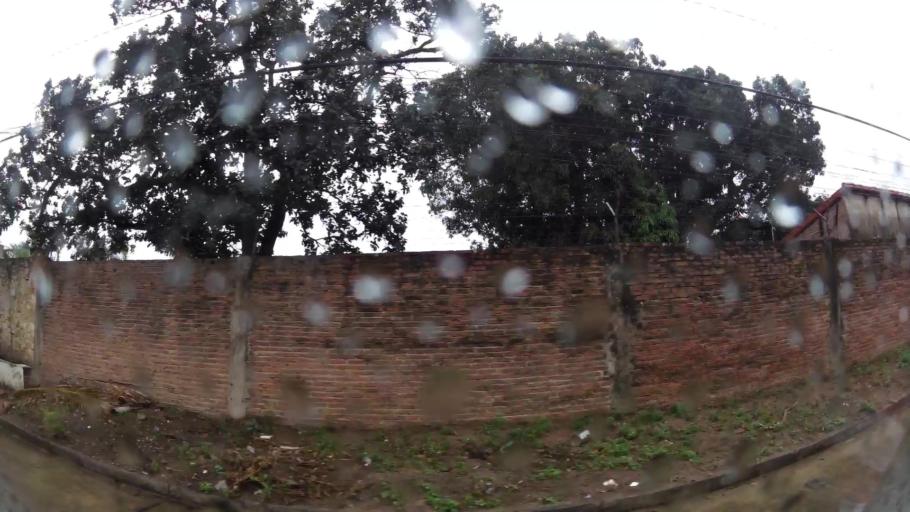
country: BO
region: Santa Cruz
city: Santa Cruz de la Sierra
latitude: -17.7869
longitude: -63.2145
